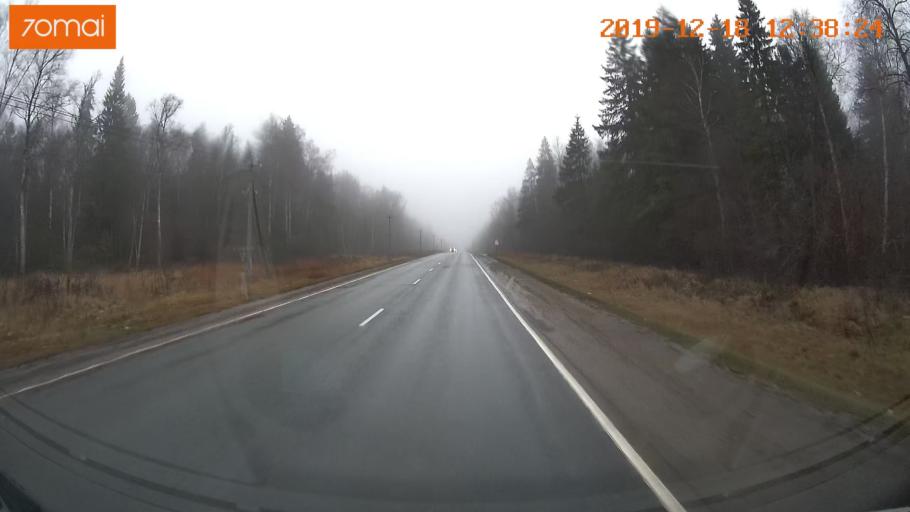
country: RU
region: Moskovskaya
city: Vysokovsk
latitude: 56.1513
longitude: 36.6047
